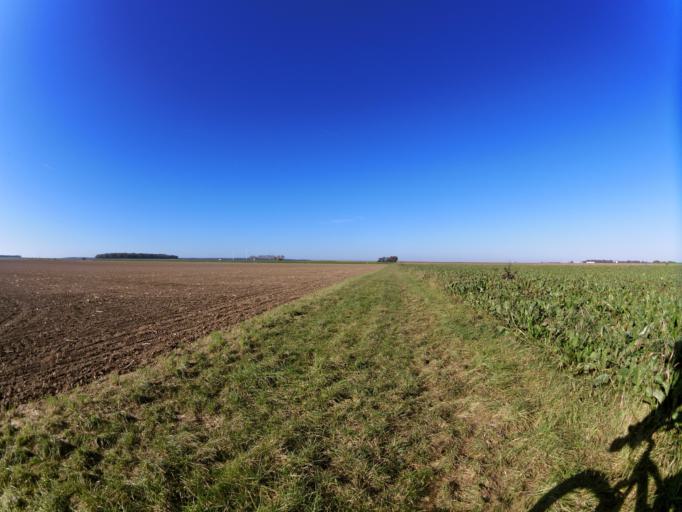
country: DE
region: Bavaria
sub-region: Regierungsbezirk Unterfranken
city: Giebelstadt
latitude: 49.6639
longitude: 9.9374
